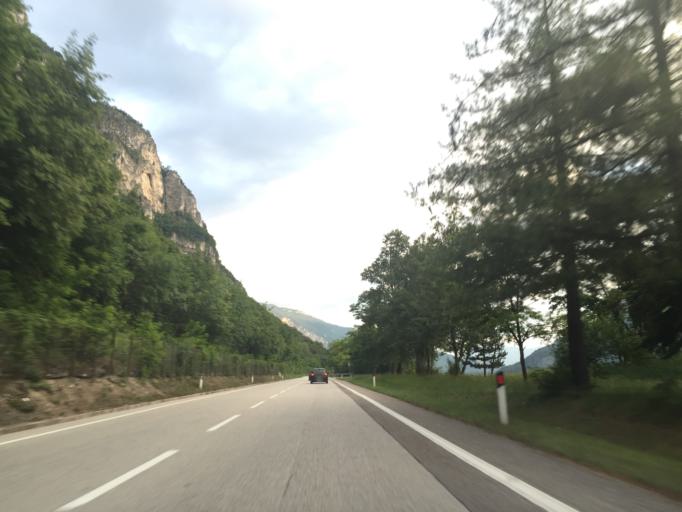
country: IT
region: Trentino-Alto Adige
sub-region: Provincia di Trento
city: Besenello
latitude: 45.9659
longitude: 11.1123
